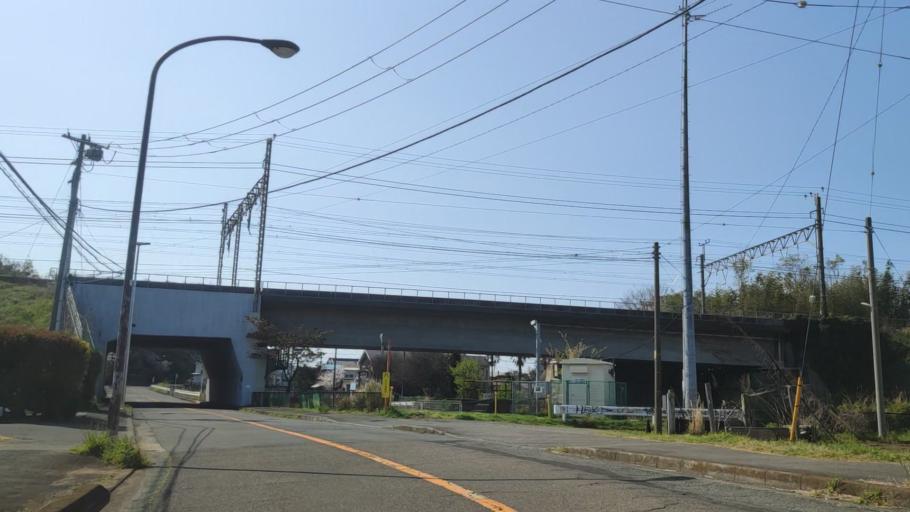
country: JP
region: Kanagawa
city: Oiso
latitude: 35.3074
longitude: 139.2884
